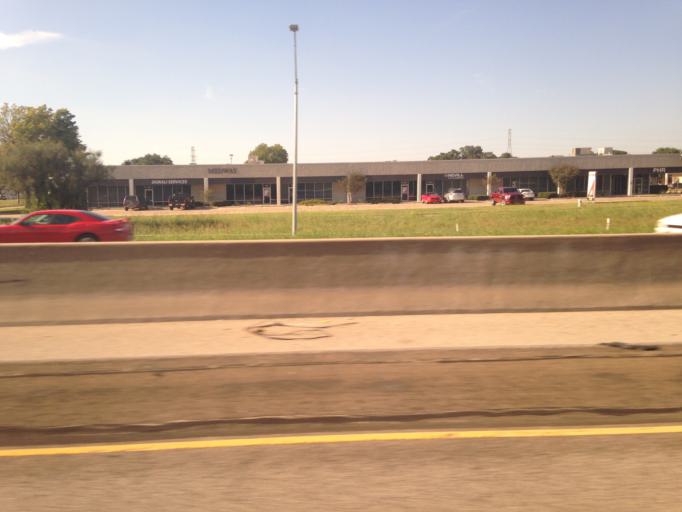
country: US
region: Texas
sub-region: Tarrant County
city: Richland Hills
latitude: 32.8021
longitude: -97.2188
